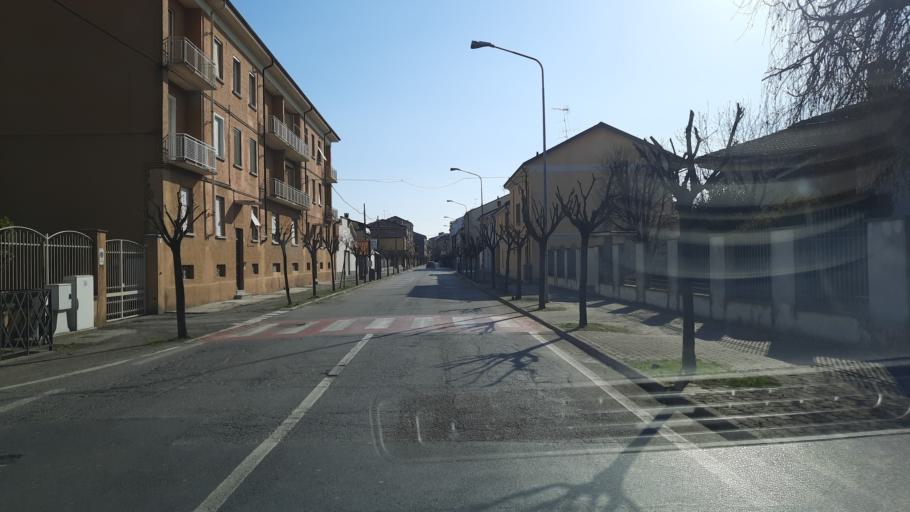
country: IT
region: Piedmont
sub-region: Provincia di Vercelli
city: Trino
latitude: 45.2016
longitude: 8.2986
